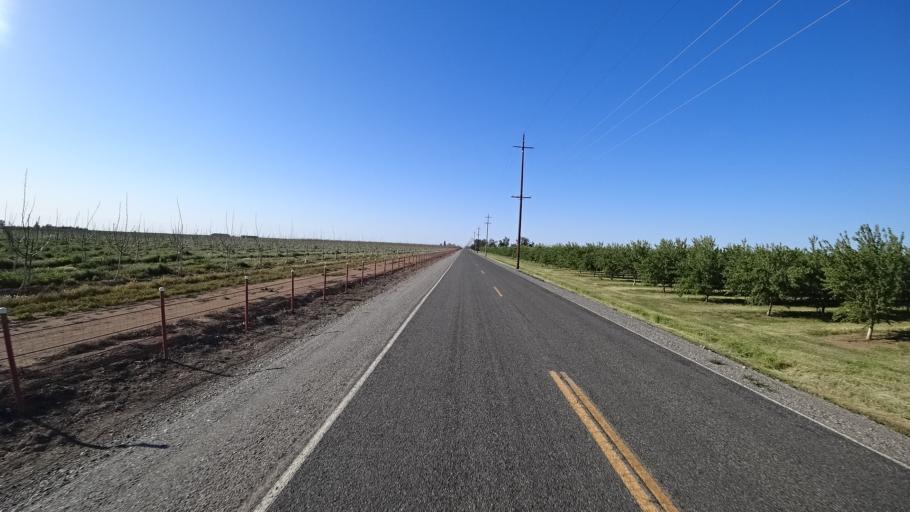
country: US
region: California
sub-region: Glenn County
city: Orland
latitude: 39.6951
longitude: -122.1779
